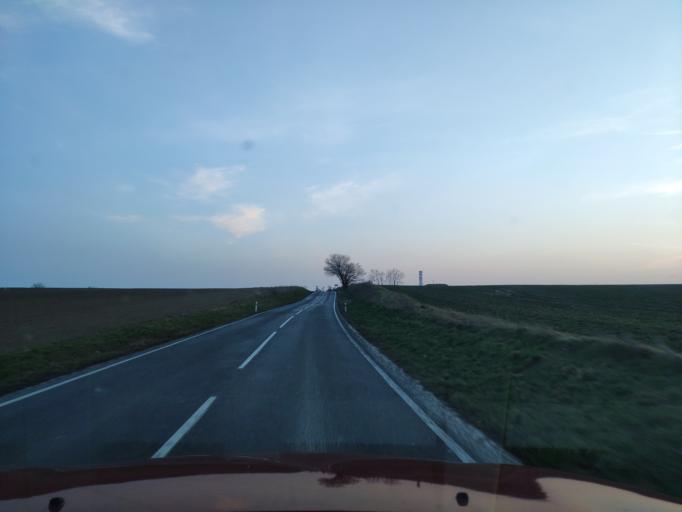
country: SK
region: Trnavsky
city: Leopoldov
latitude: 48.4678
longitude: 17.7024
